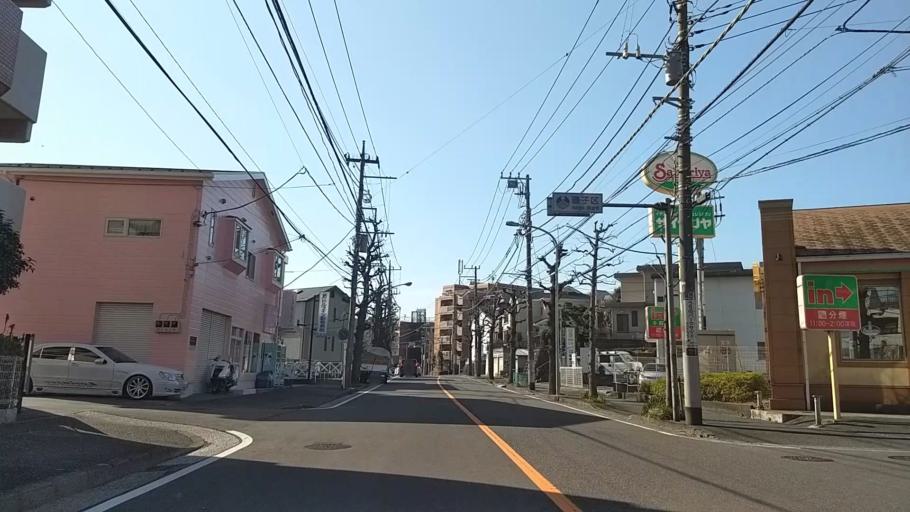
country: JP
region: Kanagawa
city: Yokohama
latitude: 35.3881
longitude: 139.6017
